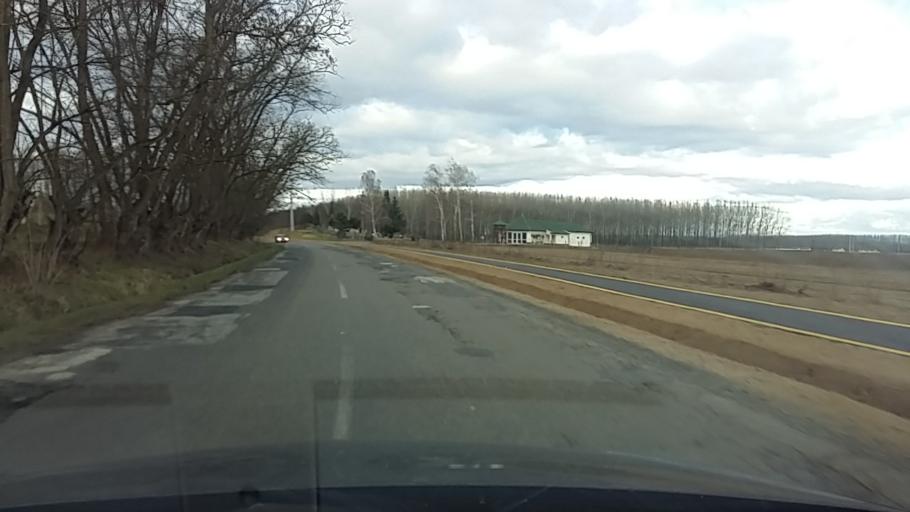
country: HU
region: Szabolcs-Szatmar-Bereg
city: Nyirbogdany
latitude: 48.0663
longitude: 21.8607
